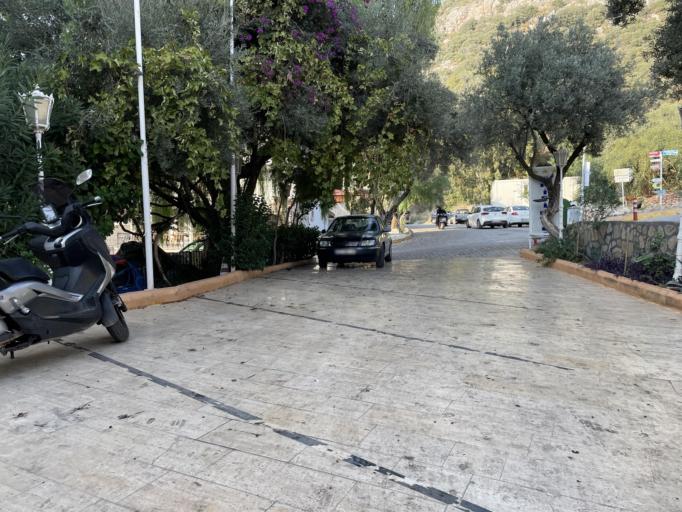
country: TR
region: Antalya
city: Kas
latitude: 36.1991
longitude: 29.6440
